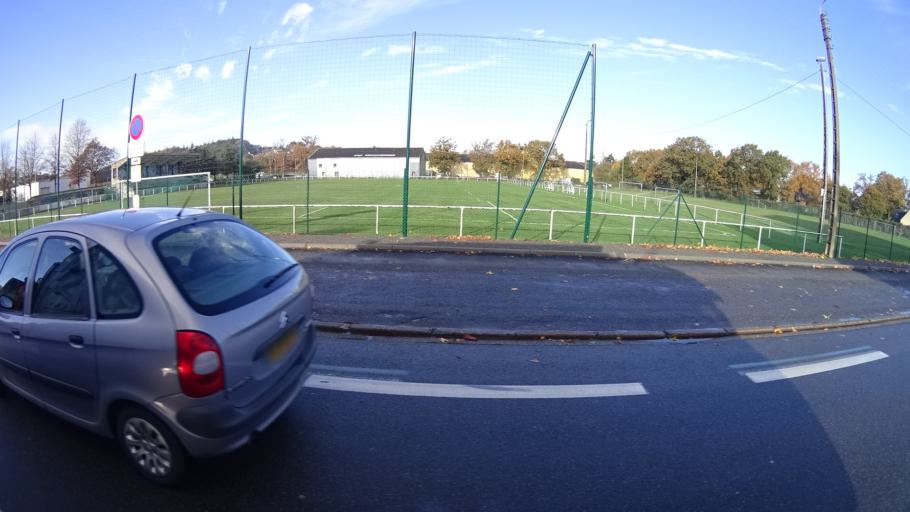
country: FR
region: Brittany
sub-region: Departement d'Ille-et-Vilaine
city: Redon
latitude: 47.6639
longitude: -2.0726
